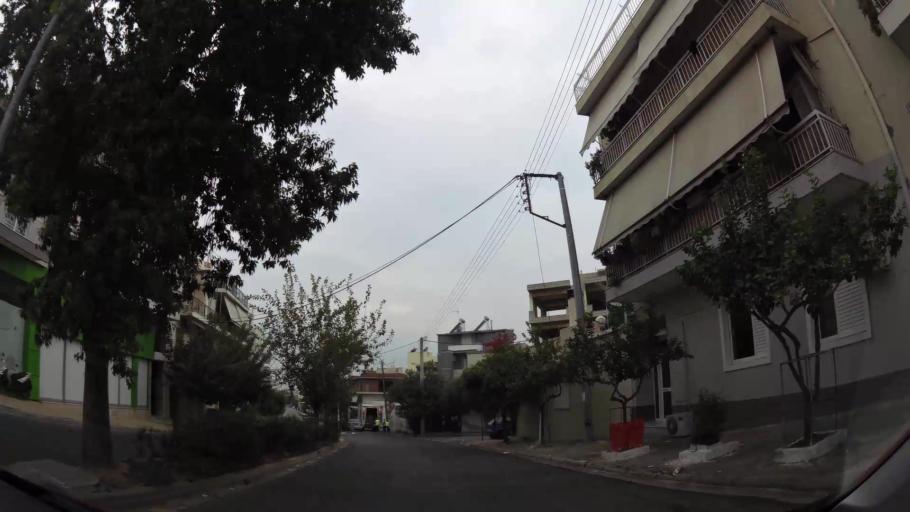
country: GR
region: Attica
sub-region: Nomarchia Athinas
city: Ilion
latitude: 38.0229
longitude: 23.6997
